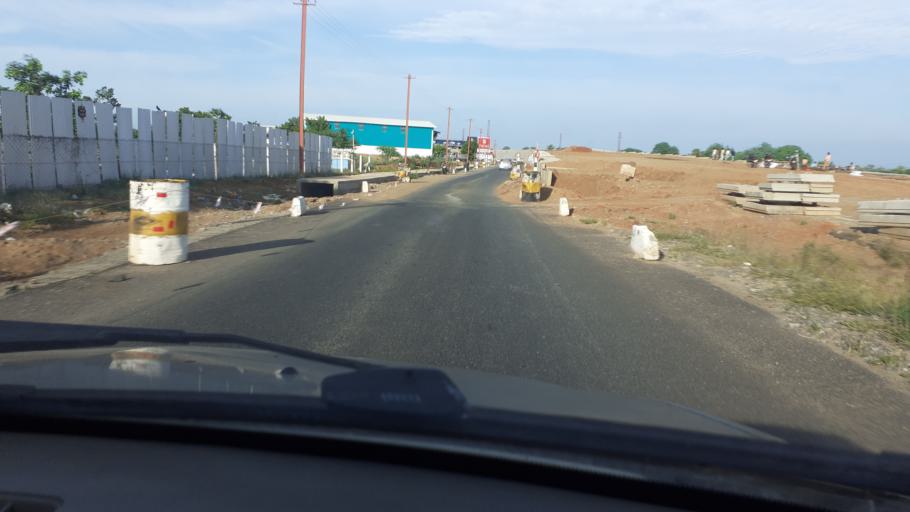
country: IN
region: Tamil Nadu
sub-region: Tirunelveli Kattabo
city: Tirunelveli
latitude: 8.6218
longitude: 77.6921
